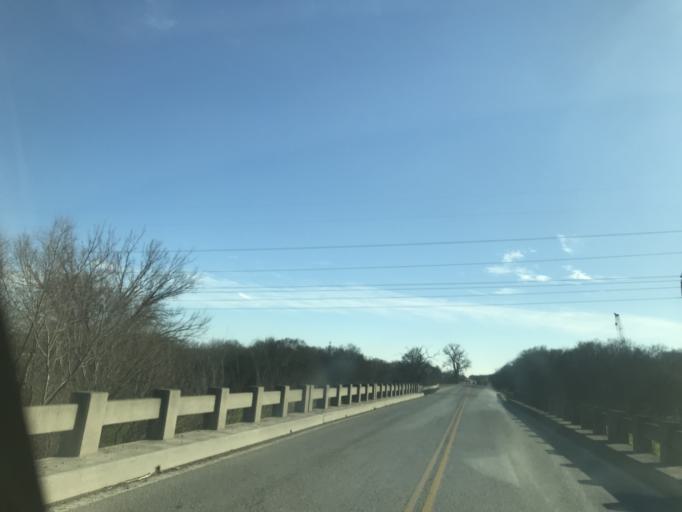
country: US
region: Texas
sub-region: Ellis County
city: Ferris
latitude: 32.5594
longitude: -96.6657
